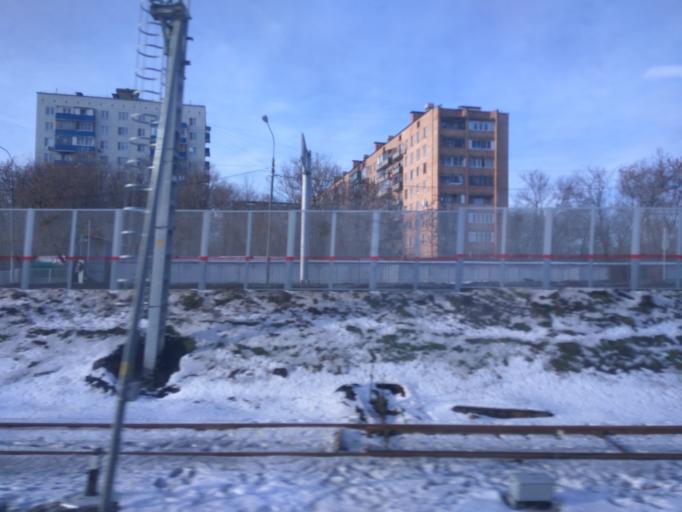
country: RU
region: Moskovskaya
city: Bogorodskoye
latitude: 55.7999
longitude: 37.7461
